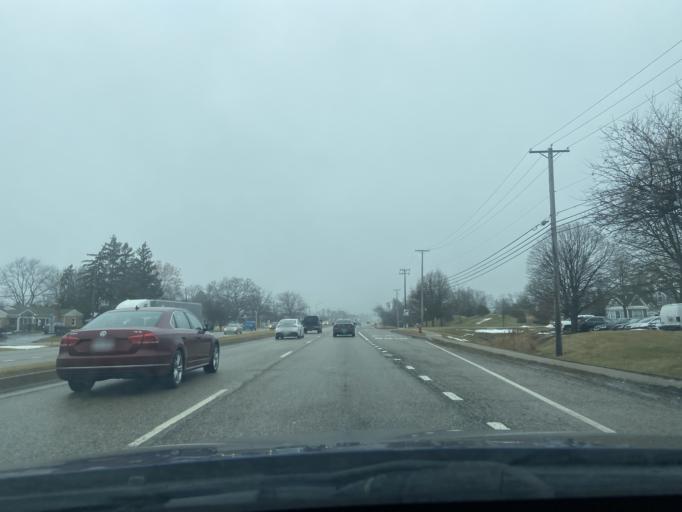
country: US
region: Illinois
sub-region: Lake County
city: Knollwood
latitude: 42.1997
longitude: -88.1114
